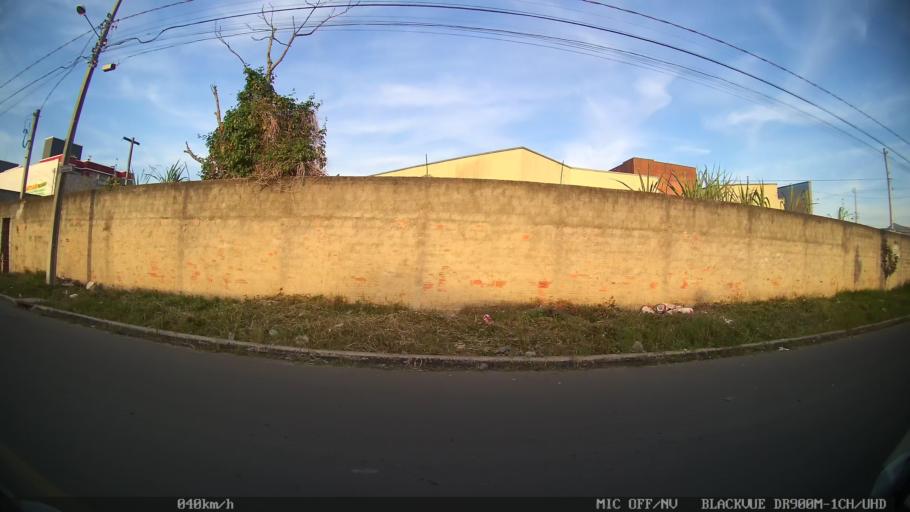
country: BR
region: Parana
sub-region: Pinhais
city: Pinhais
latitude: -25.4519
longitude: -49.1717
